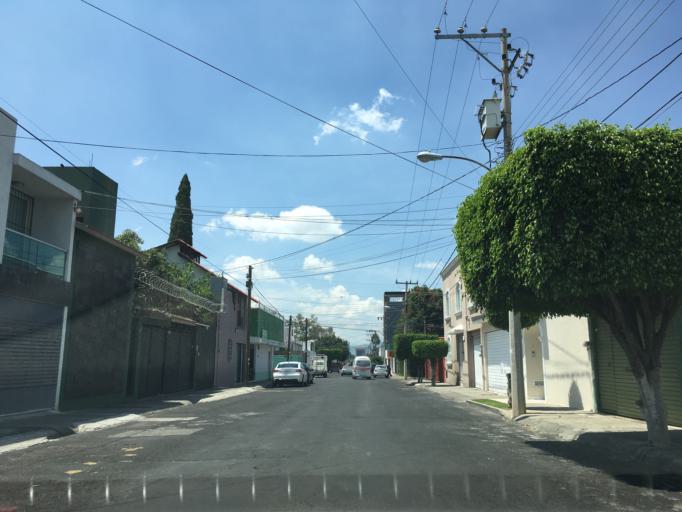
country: MX
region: Michoacan
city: Morelia
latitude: 19.6873
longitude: -101.1654
